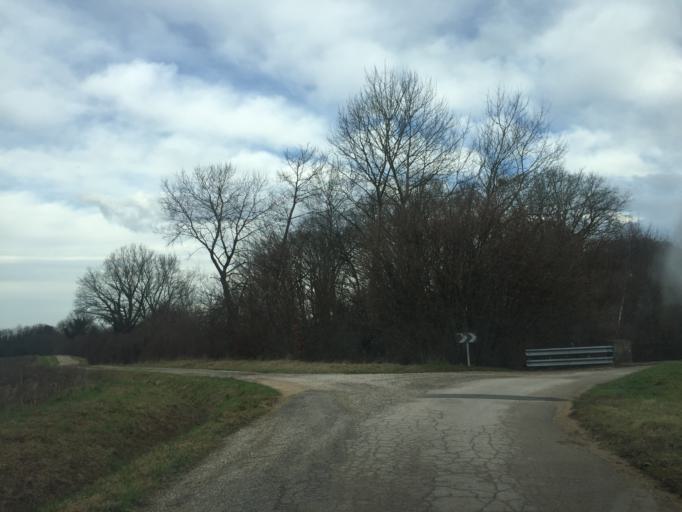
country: FR
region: Franche-Comte
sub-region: Departement du Jura
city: Chaussin
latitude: 46.9093
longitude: 5.4654
